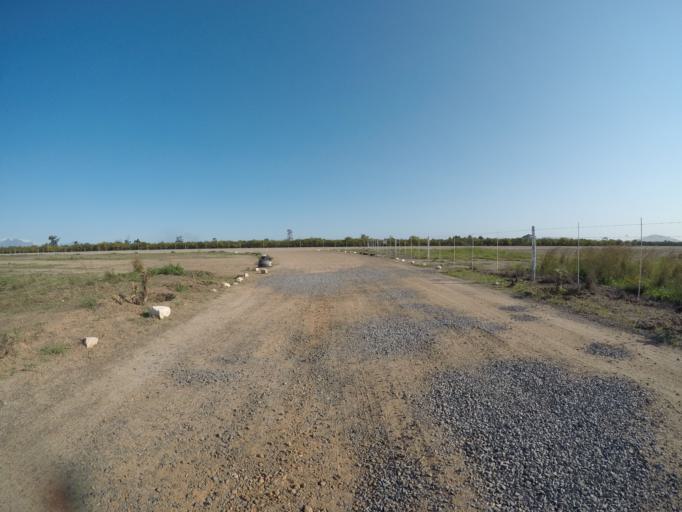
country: ZA
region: Western Cape
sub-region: City of Cape Town
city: Kraaifontein
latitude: -33.7717
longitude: 18.7432
